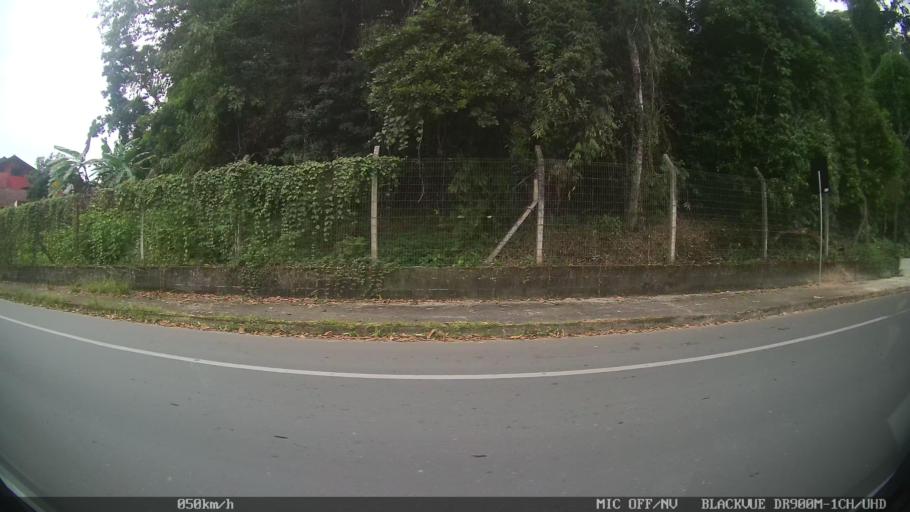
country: BR
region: Santa Catarina
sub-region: Joinville
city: Joinville
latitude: -26.3276
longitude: -48.8495
